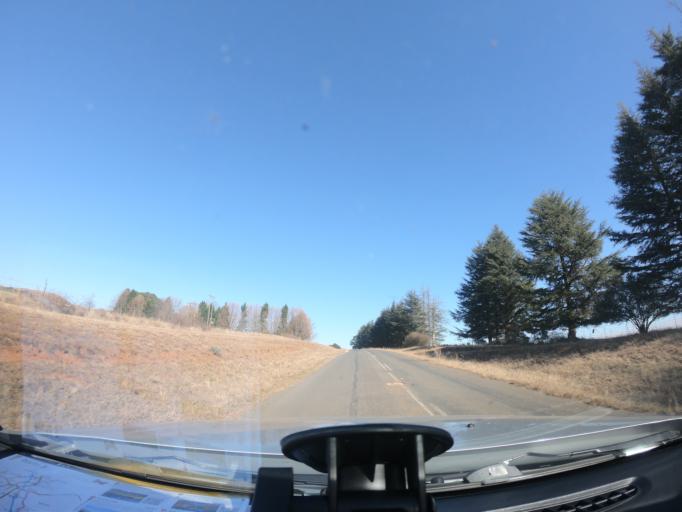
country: ZA
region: KwaZulu-Natal
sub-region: uMgungundlovu District Municipality
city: Mooirivier
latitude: -29.3280
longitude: 29.8253
